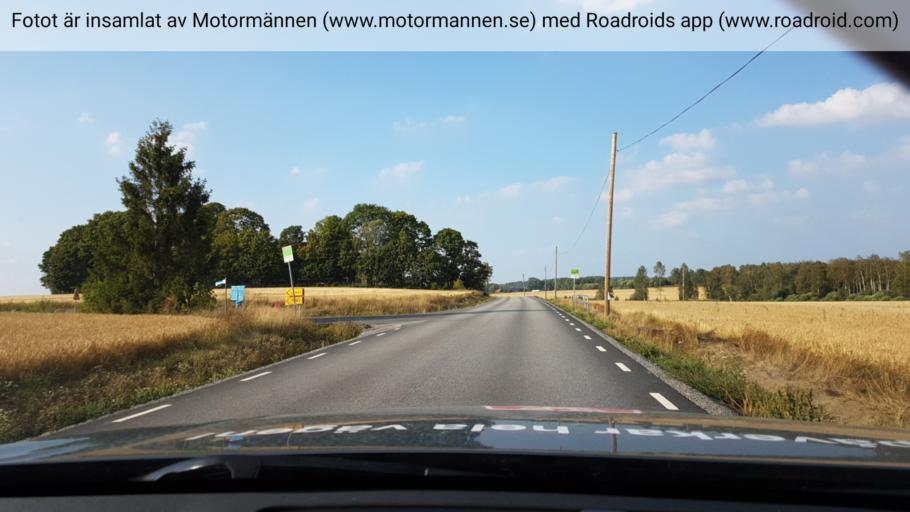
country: SE
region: Soedermanland
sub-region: Gnesta Kommun
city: Gnesta
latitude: 59.1304
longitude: 17.2148
